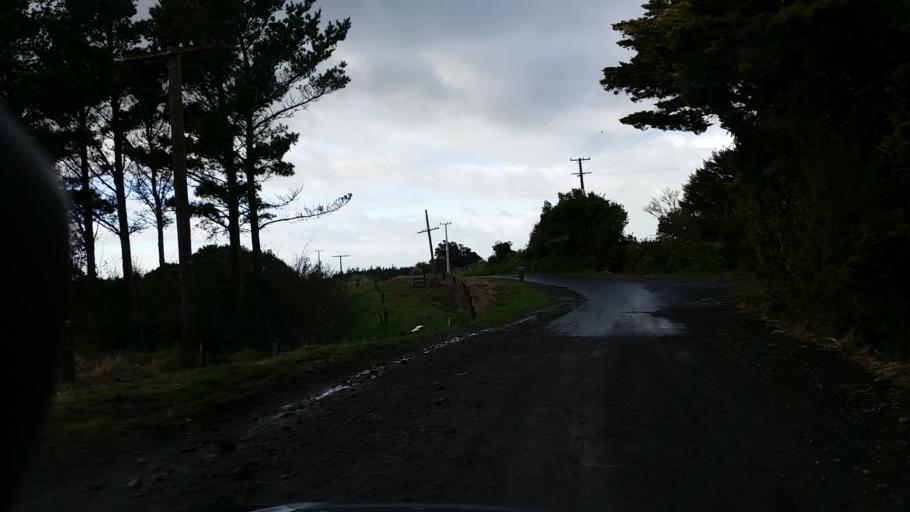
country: NZ
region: Taranaki
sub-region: South Taranaki District
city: Eltham
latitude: -39.3384
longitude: 174.1859
